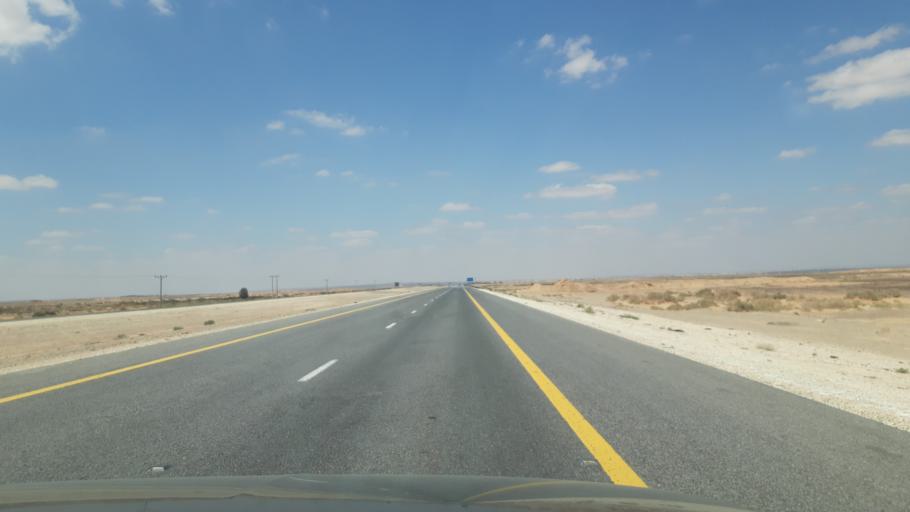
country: JO
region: Amman
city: Al Azraq ash Shamali
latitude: 31.7167
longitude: 36.8491
